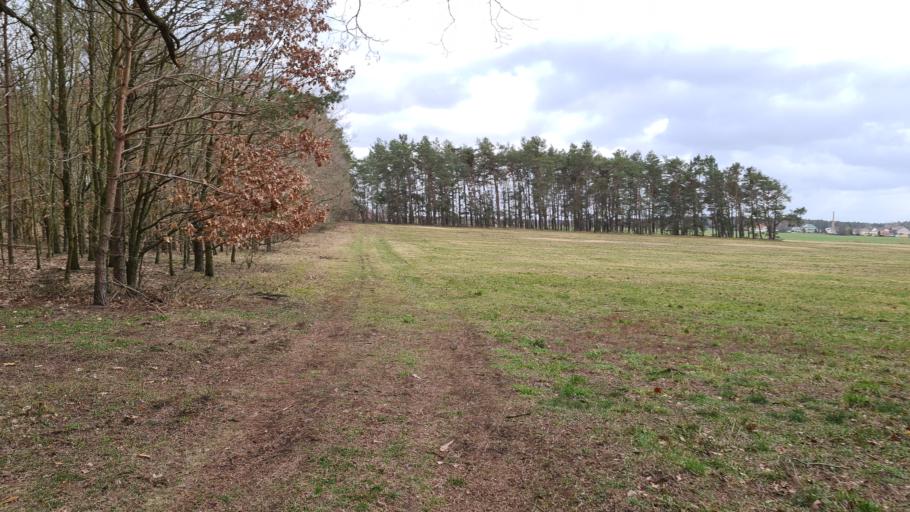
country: DE
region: Brandenburg
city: Schilda
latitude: 51.6116
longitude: 13.3975
